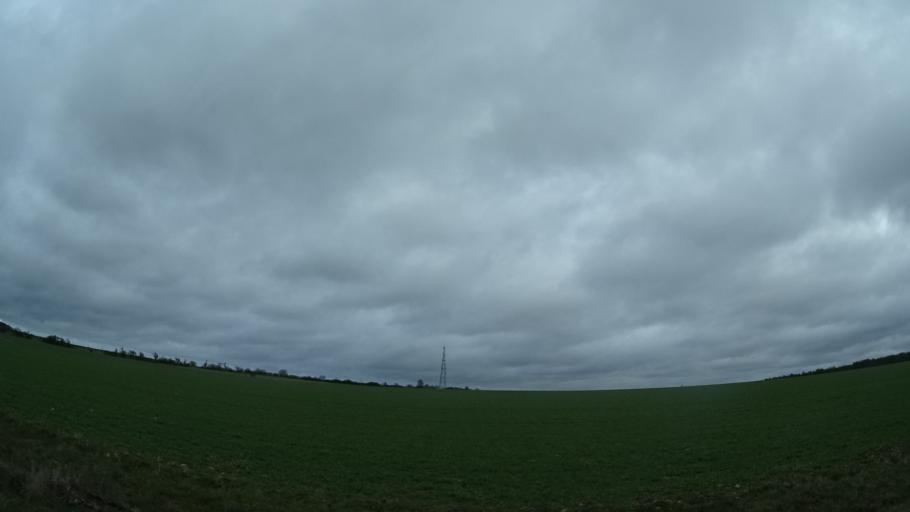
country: DE
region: Thuringia
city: Nauendorf
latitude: 50.9100
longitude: 11.1913
